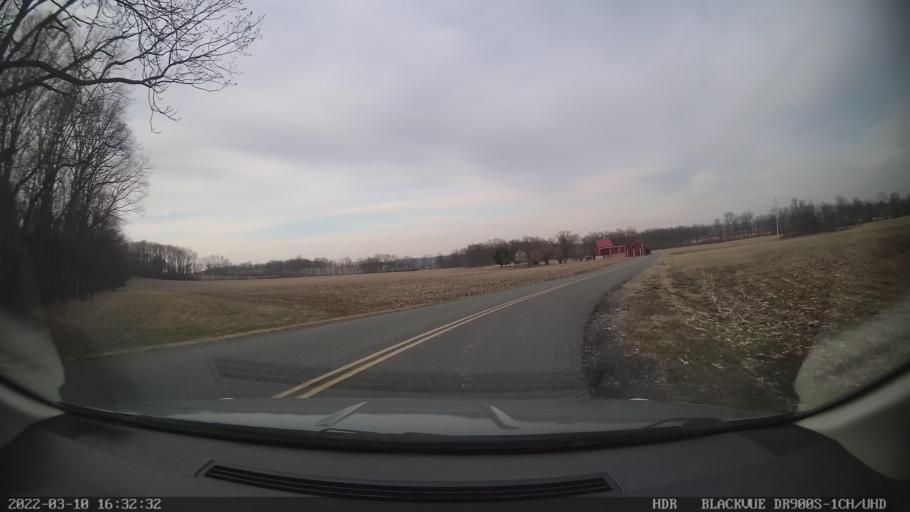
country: US
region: Pennsylvania
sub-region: Berks County
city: Oley
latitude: 40.3629
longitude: -75.7882
